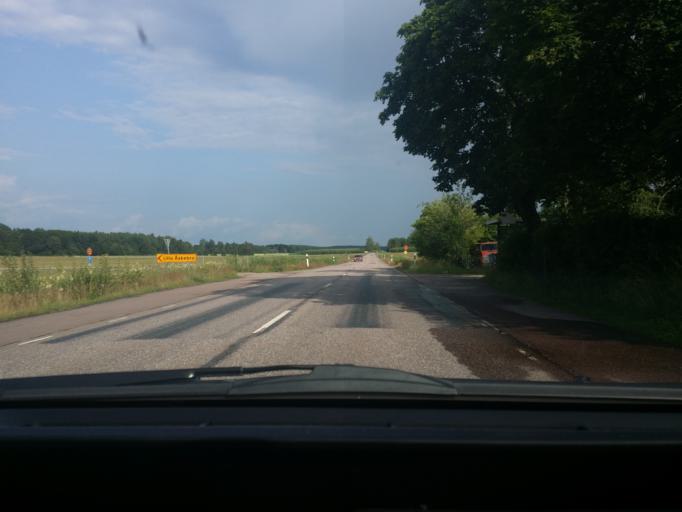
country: SE
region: Vaestmanland
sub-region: Hallstahammars Kommun
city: Kolback
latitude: 59.5621
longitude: 16.3137
